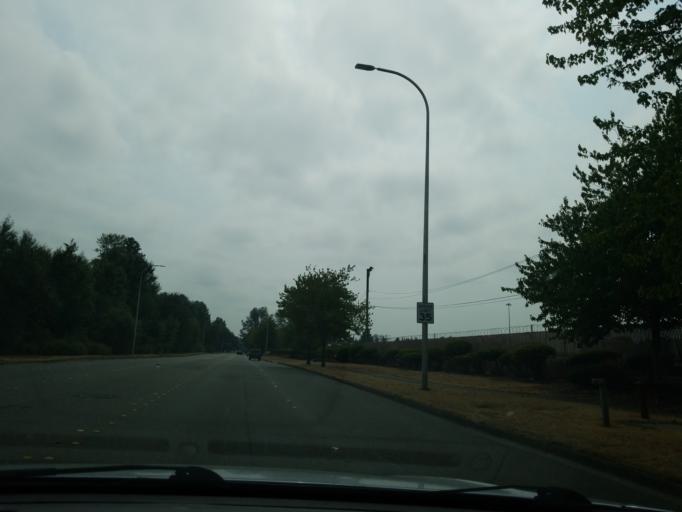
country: US
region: Washington
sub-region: King County
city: Renton
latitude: 47.4484
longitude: -122.2328
